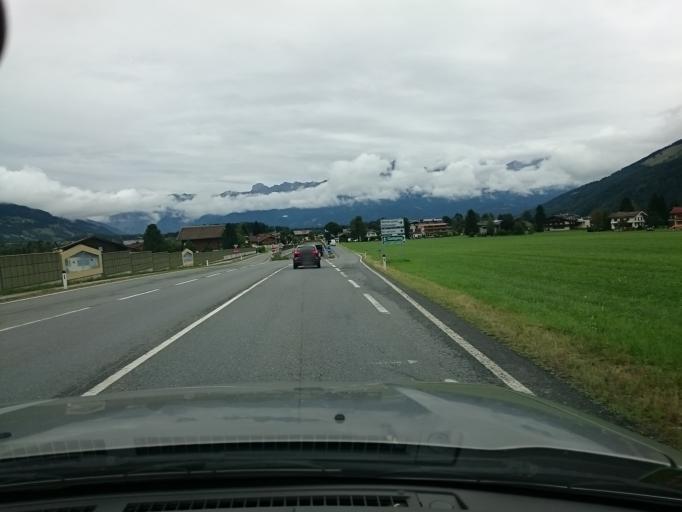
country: AT
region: Salzburg
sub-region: Politischer Bezirk Zell am See
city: Maishofen
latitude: 47.3646
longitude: 12.8019
